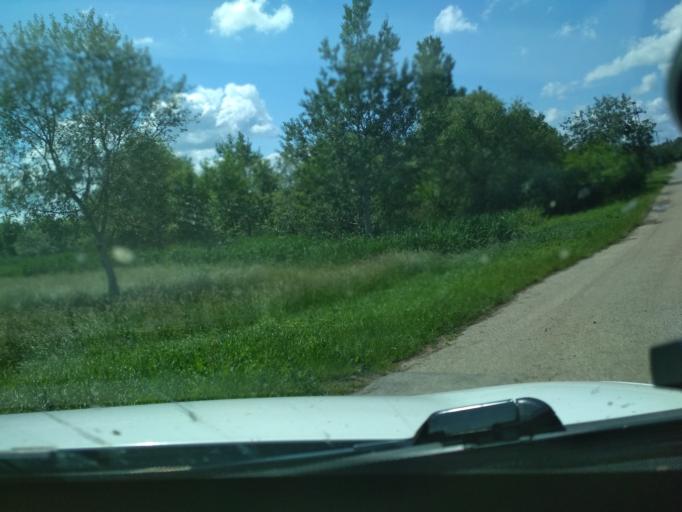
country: HU
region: Jasz-Nagykun-Szolnok
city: Abadszalok
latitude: 47.4829
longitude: 20.6067
